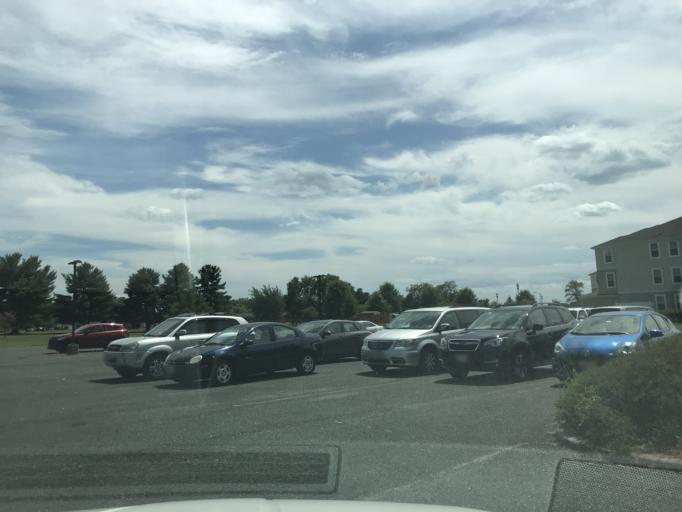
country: US
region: Maryland
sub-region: Harford County
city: Joppatowne
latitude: 39.4107
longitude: -76.3513
